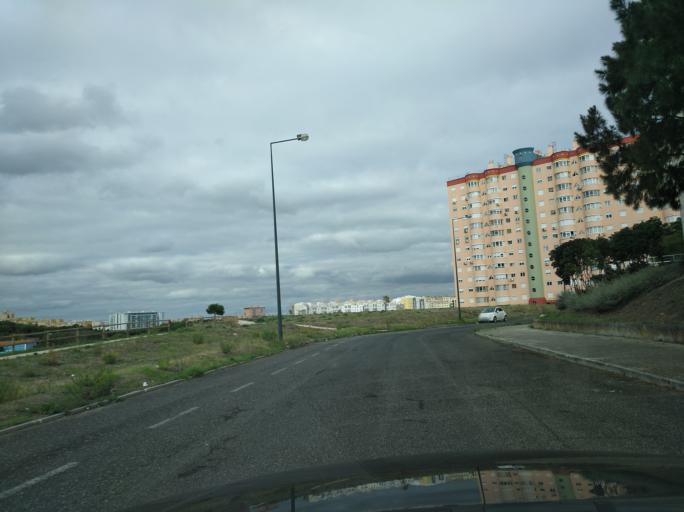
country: PT
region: Lisbon
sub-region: Lisbon
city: Lisbon
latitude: 38.7419
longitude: -9.1263
